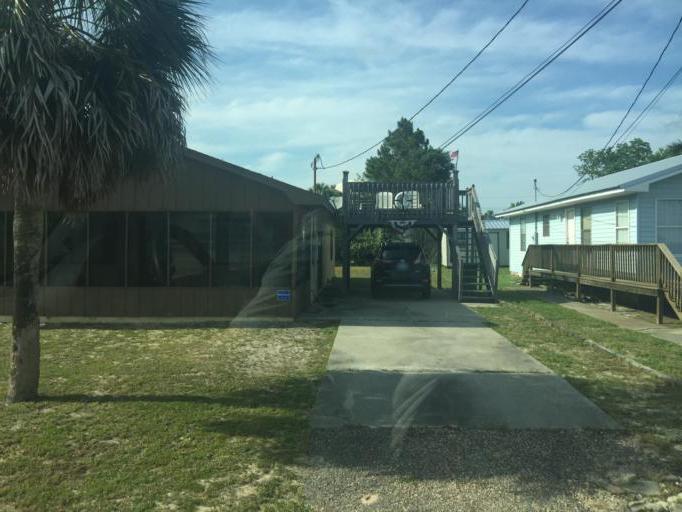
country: US
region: Florida
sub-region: Bay County
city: Laguna Beach
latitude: 30.2536
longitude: -85.9514
